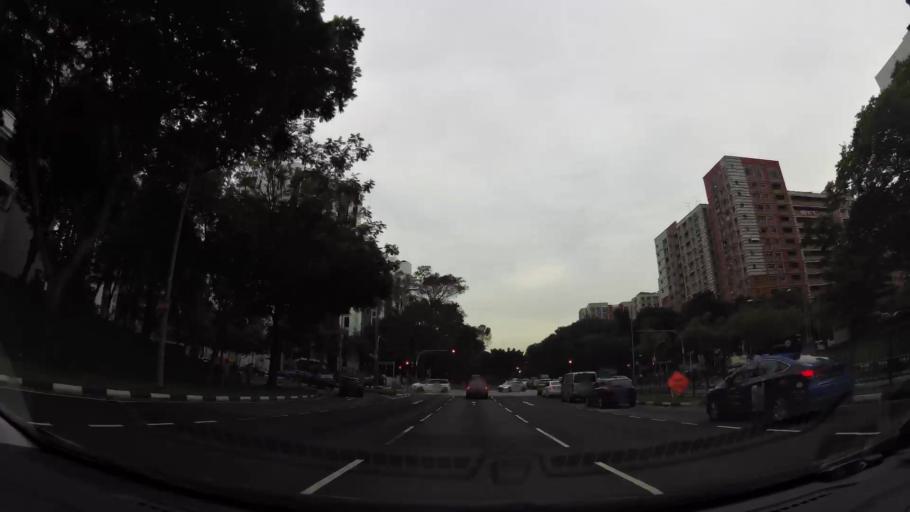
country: SG
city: Singapore
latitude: 1.3754
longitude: 103.8771
